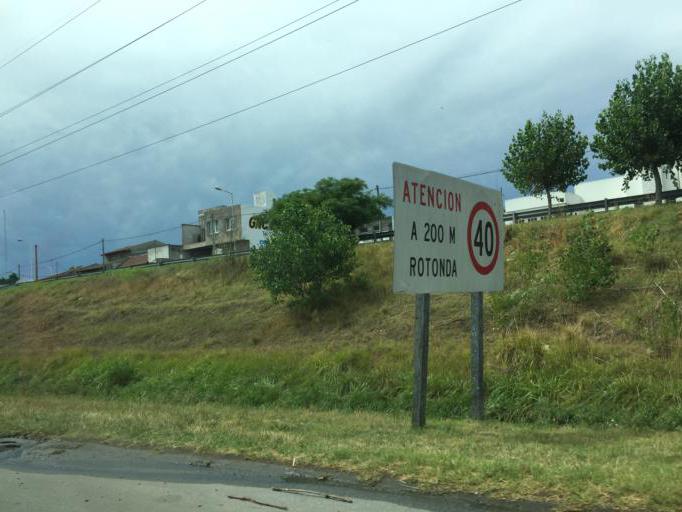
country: AR
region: Buenos Aires
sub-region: Partido de Tandil
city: Tandil
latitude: -37.3006
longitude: -59.1281
